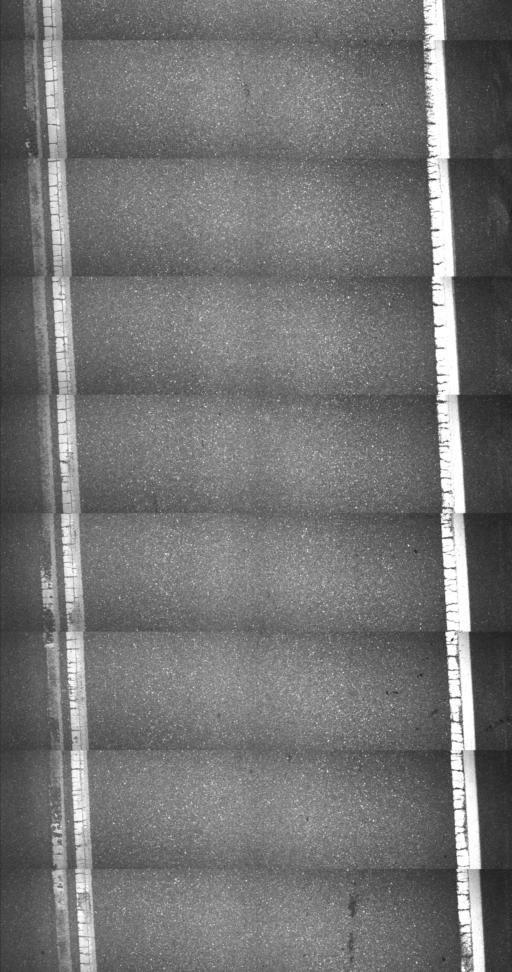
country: US
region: Vermont
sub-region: Windham County
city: Brattleboro
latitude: 42.7746
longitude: -72.5669
